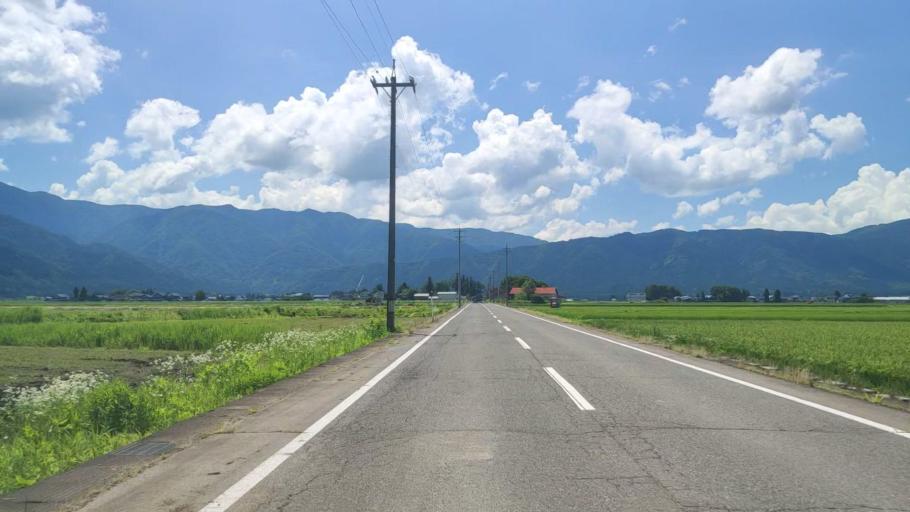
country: JP
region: Fukui
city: Ono
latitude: 35.9665
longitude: 136.5287
